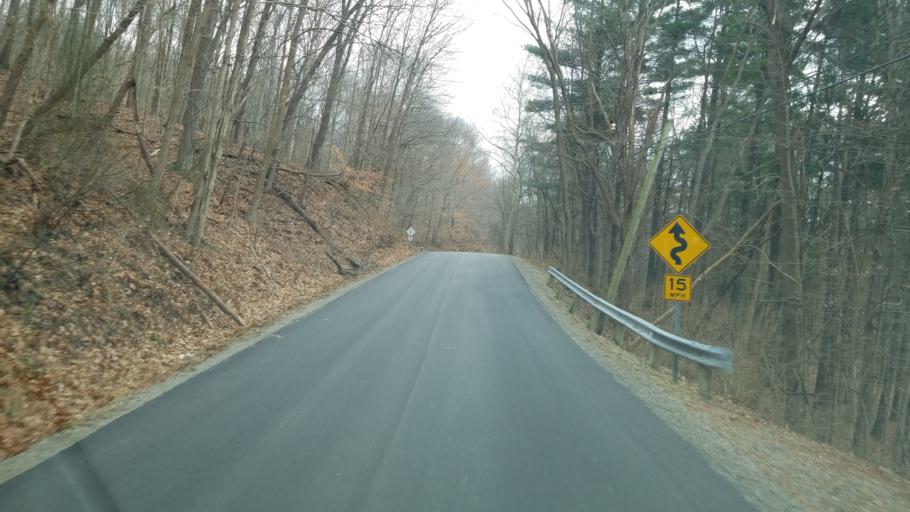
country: US
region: Ohio
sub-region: Highland County
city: Greenfield
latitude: 39.2150
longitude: -83.2687
